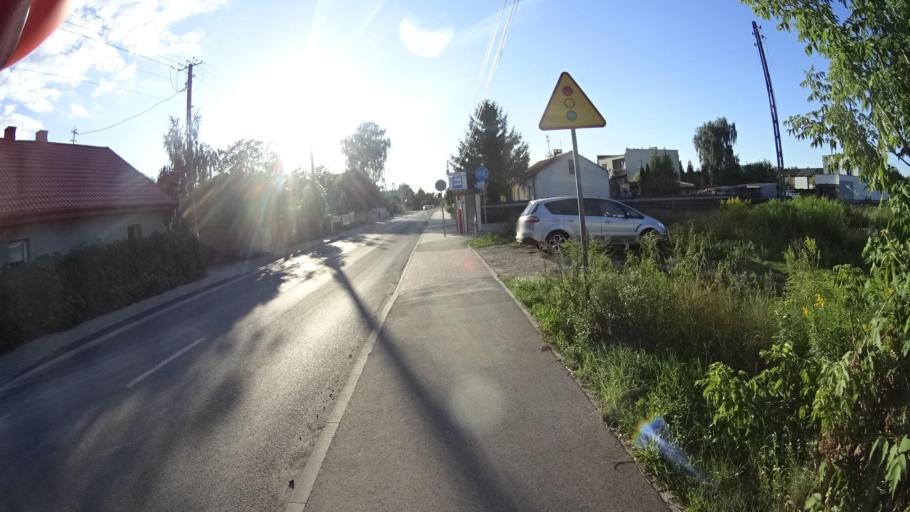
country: PL
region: Masovian Voivodeship
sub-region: Powiat pruszkowski
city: Rybie
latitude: 52.1465
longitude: 20.9474
